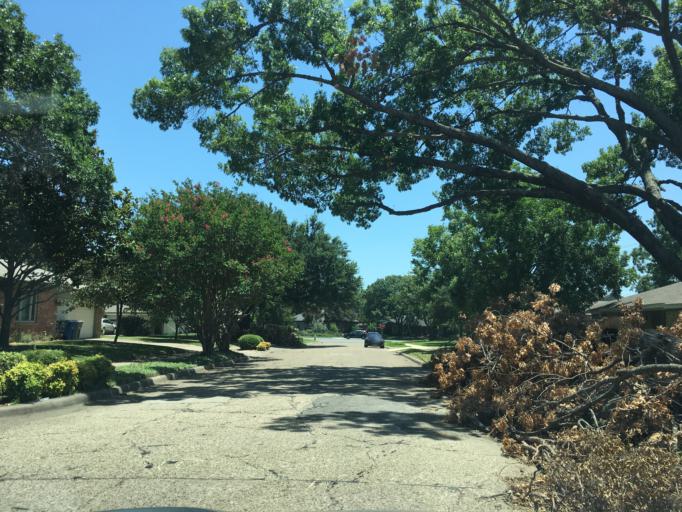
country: US
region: Texas
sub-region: Dallas County
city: Highland Park
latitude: 32.8407
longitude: -96.7457
